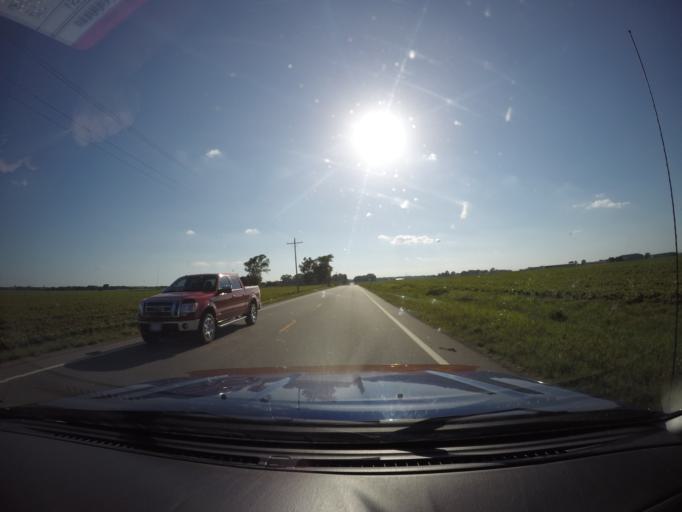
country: US
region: Kansas
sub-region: Douglas County
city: Lawrence
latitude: 39.0006
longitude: -95.2127
